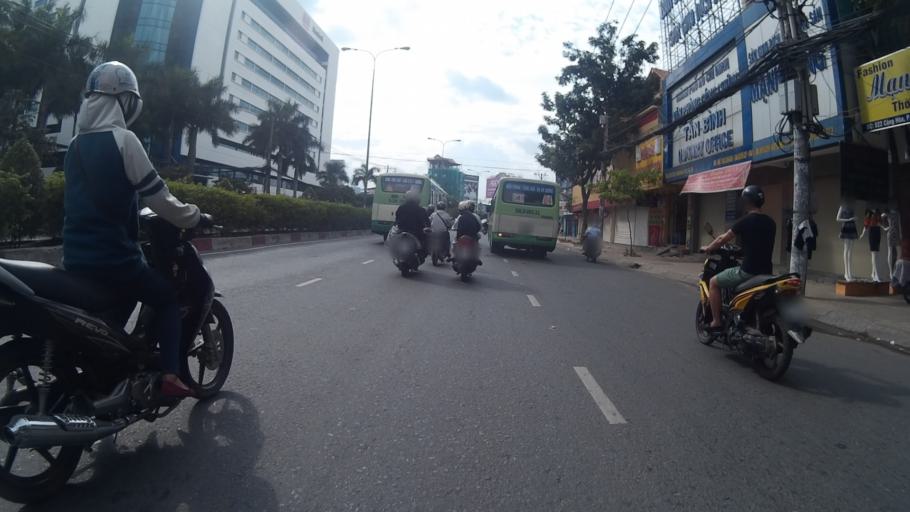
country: VN
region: Ho Chi Minh City
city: Quan Tan Phu
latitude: 10.8025
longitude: 106.6405
